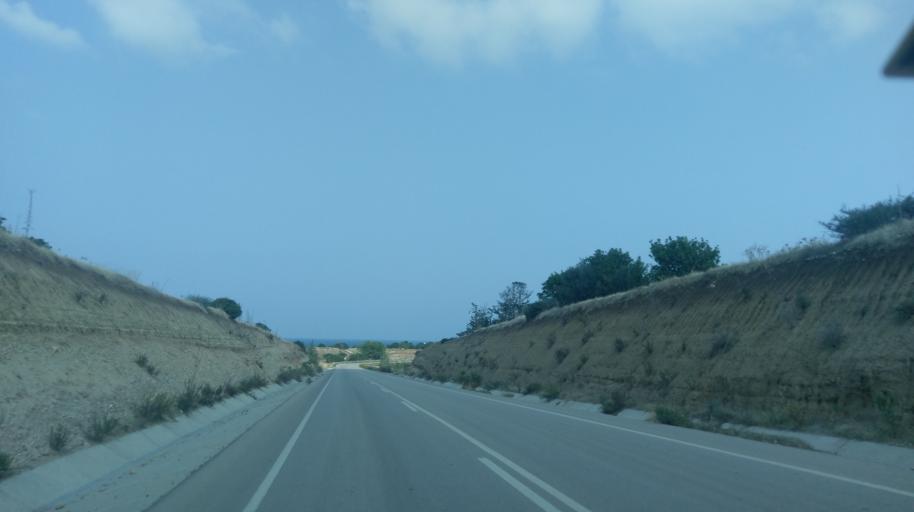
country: CY
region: Ammochostos
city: Lefkonoiko
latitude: 35.3981
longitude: 33.7599
